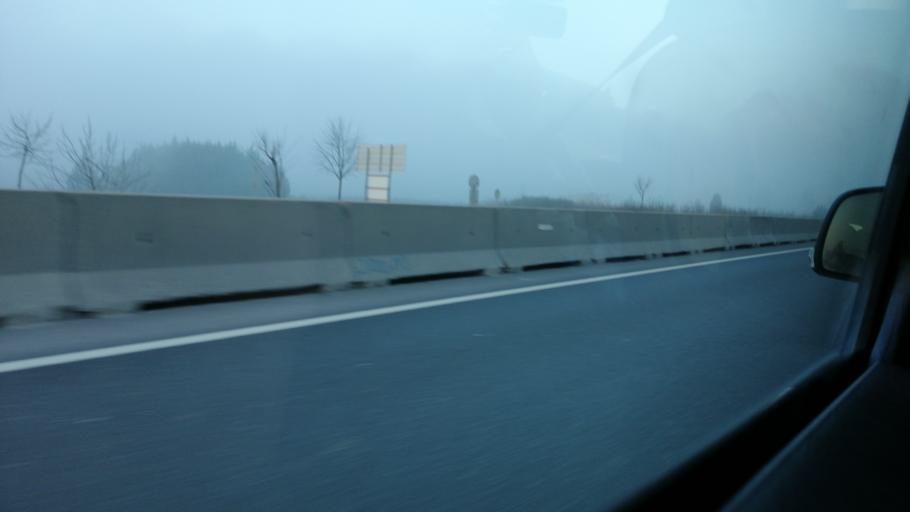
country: TR
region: Yalova
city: Taskopru
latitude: 40.6818
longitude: 29.3997
